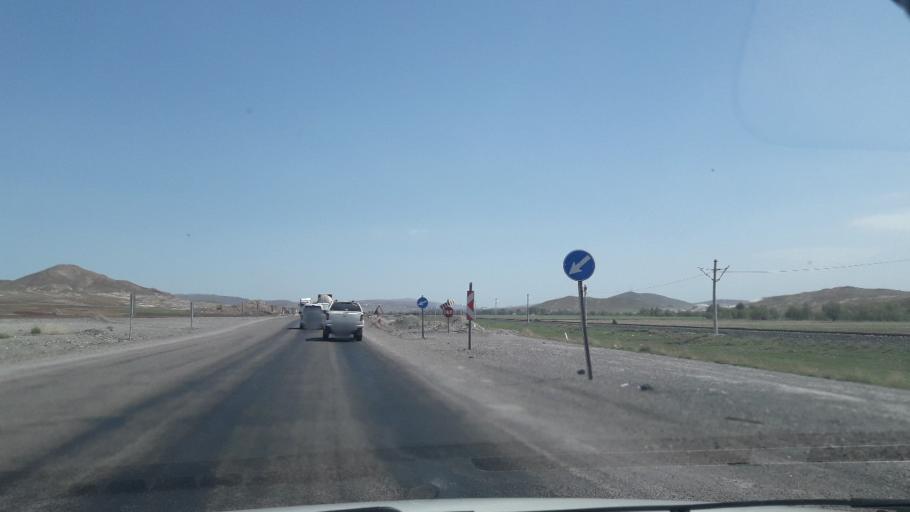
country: TR
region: Sivas
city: Ulas
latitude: 39.5263
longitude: 37.0126
